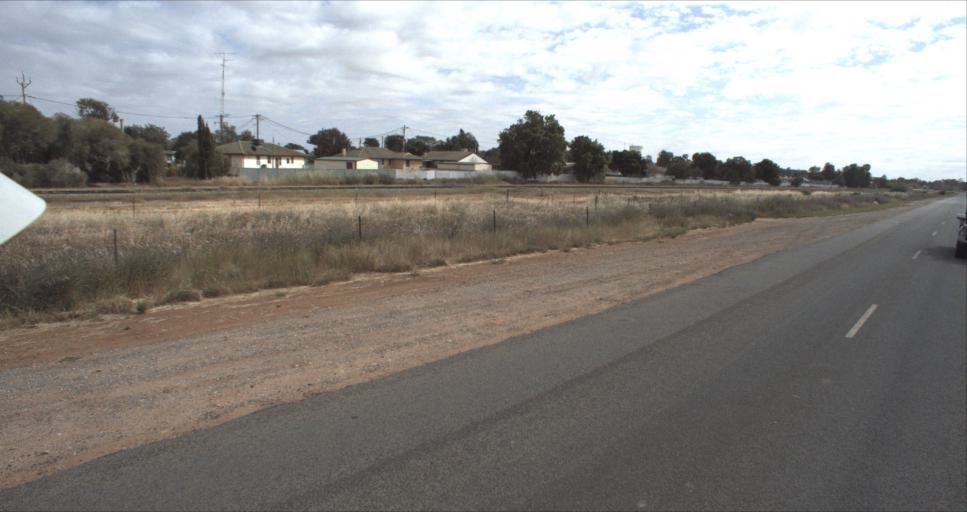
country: AU
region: New South Wales
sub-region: Leeton
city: Leeton
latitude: -34.5681
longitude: 146.3953
